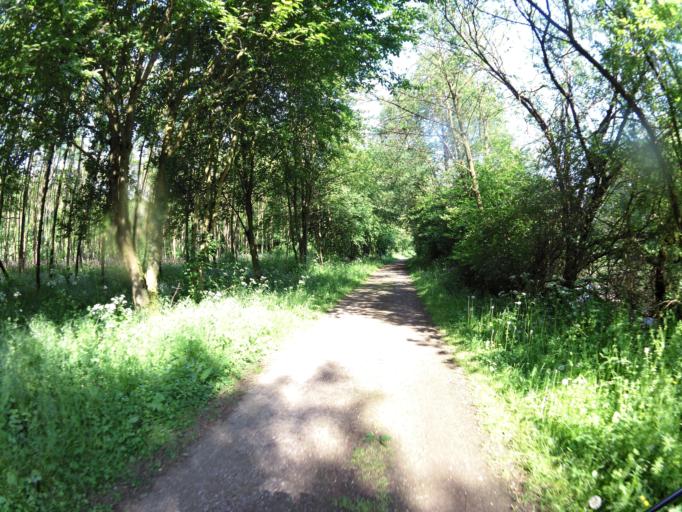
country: DE
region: North Rhine-Westphalia
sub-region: Regierungsbezirk Koln
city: Linnich
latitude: 50.9629
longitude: 6.2848
